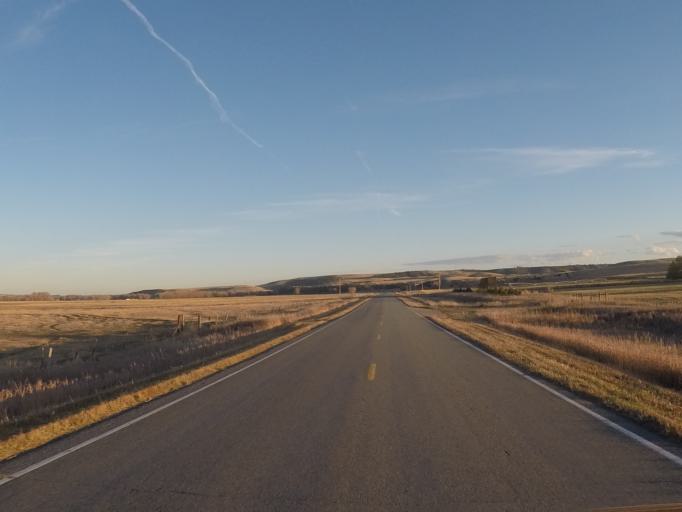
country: US
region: Montana
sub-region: Sweet Grass County
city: Big Timber
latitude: 45.7982
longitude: -109.8603
